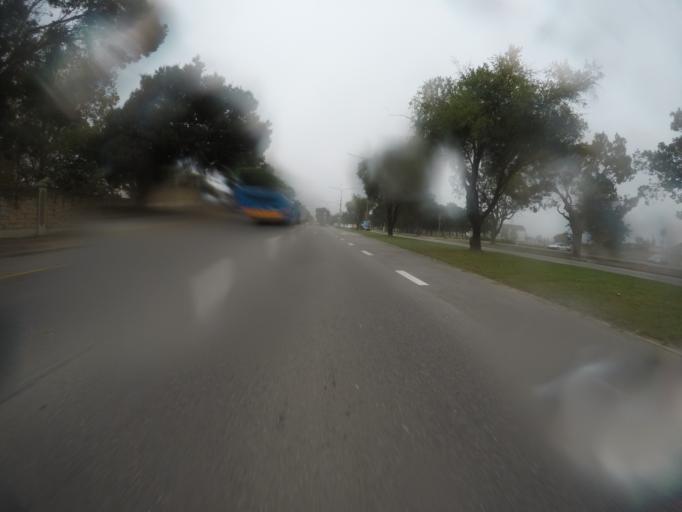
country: ZA
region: Western Cape
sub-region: Eden District Municipality
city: George
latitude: -33.9764
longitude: 22.4433
